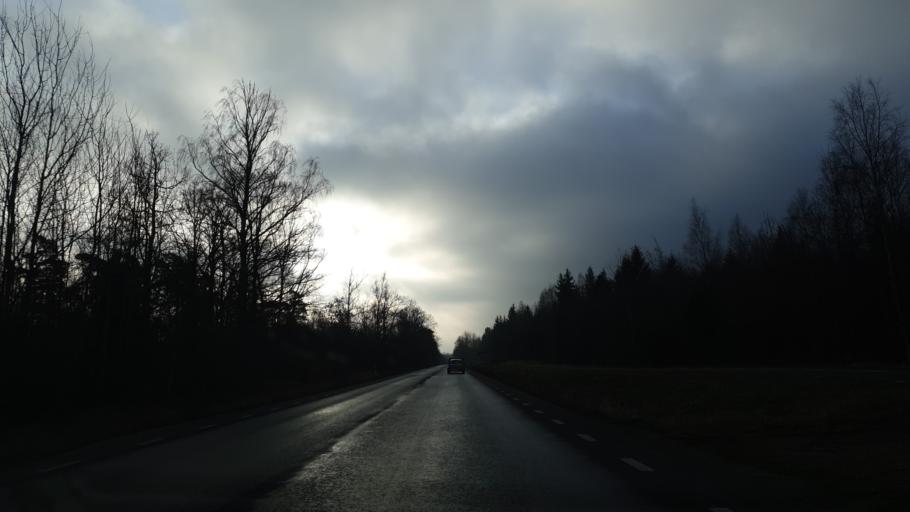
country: SE
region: Blekinge
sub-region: Karlshamns Kommun
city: Morrum
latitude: 56.1428
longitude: 14.6697
